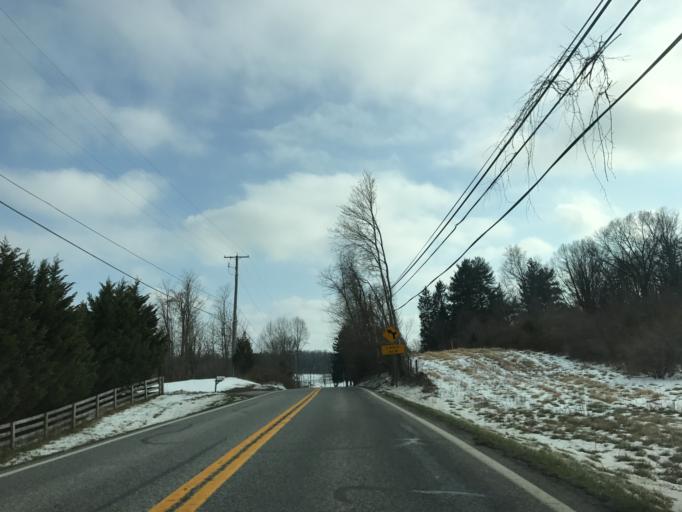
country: US
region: Maryland
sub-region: Harford County
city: South Bel Air
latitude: 39.5801
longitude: -76.2586
